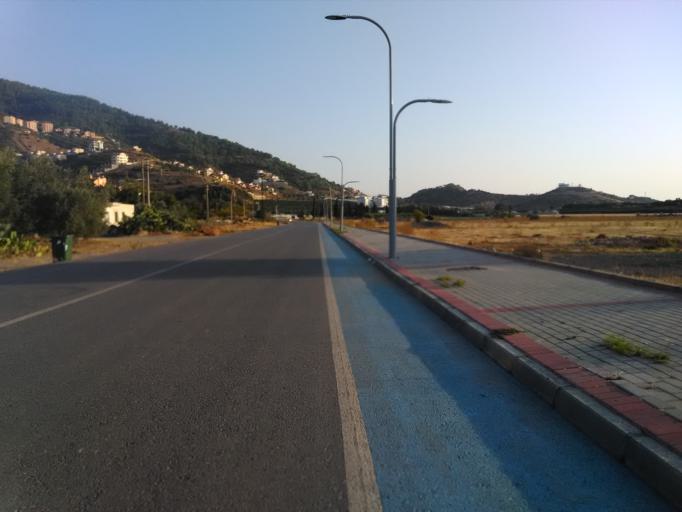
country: TR
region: Antalya
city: Gazipasa
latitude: 36.2440
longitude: 32.2973
